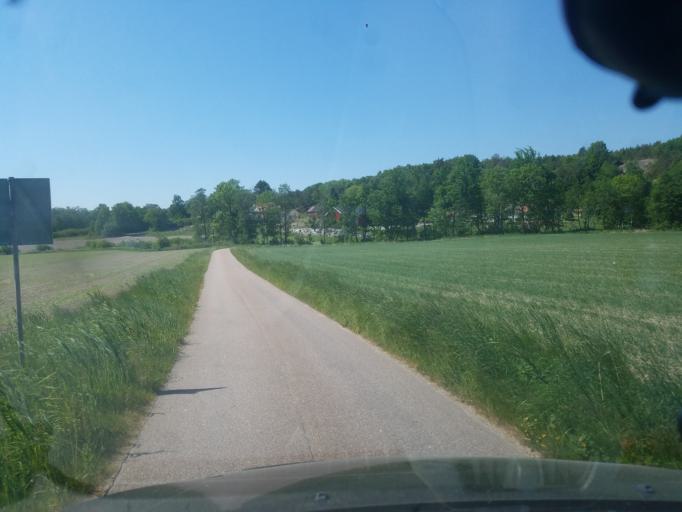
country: SE
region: Vaestra Goetaland
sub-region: Orust
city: Henan
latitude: 58.2646
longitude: 11.5729
